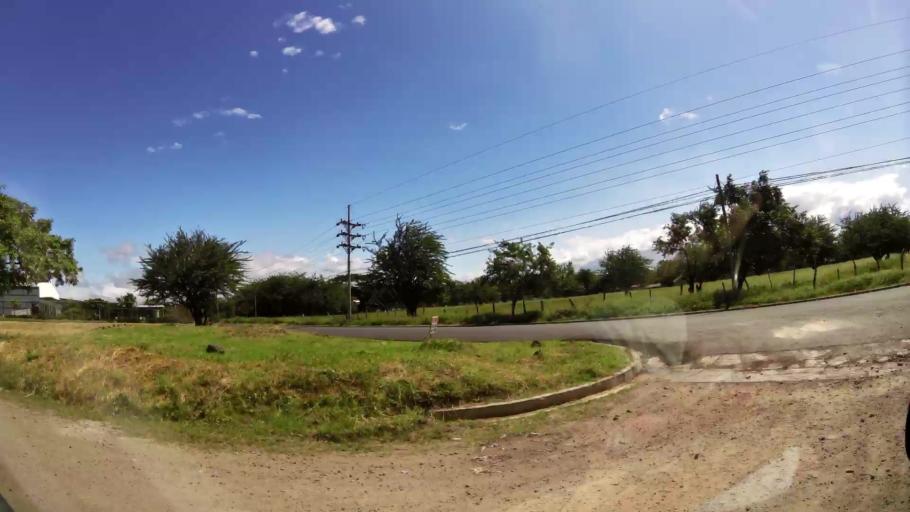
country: CR
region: Guanacaste
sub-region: Canton de Canas
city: Canas
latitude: 10.4309
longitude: -85.1024
